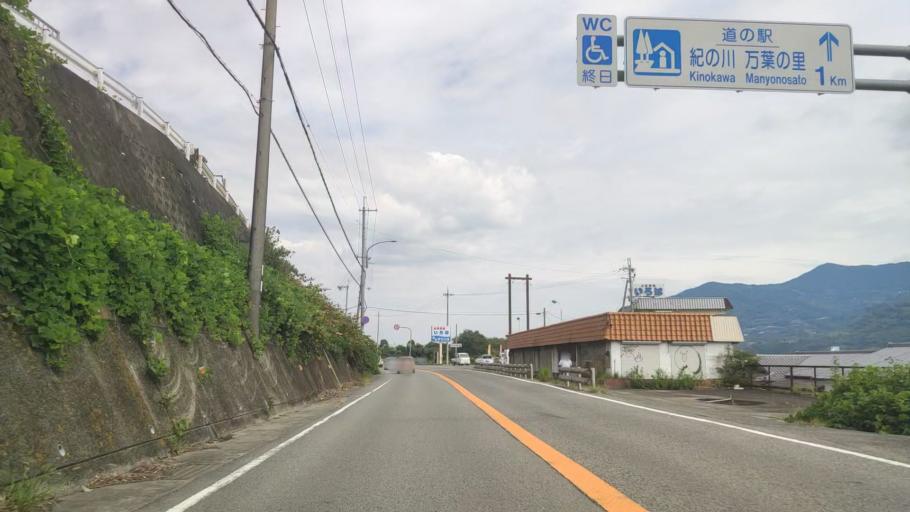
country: JP
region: Wakayama
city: Iwade
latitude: 34.2806
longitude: 135.4561
